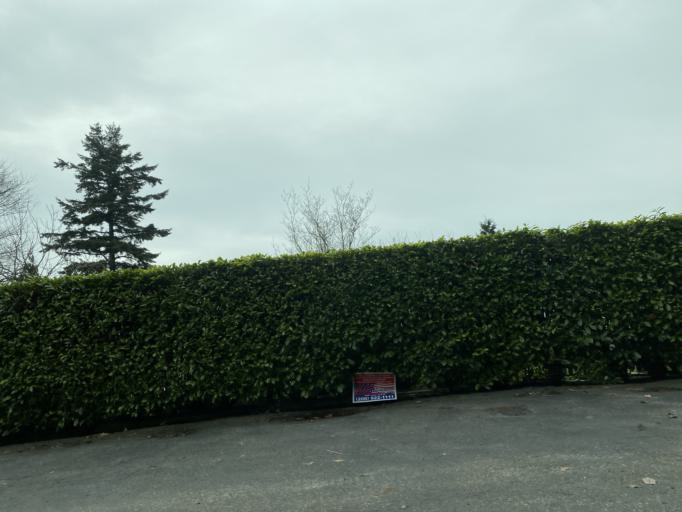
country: US
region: Washington
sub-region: King County
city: Seattle
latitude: 47.6498
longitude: -122.4162
